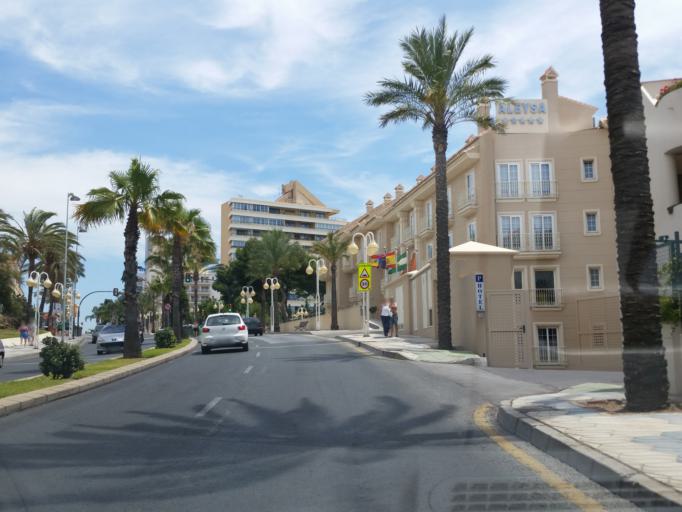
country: ES
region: Andalusia
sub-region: Provincia de Malaga
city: Torremolinos
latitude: 36.5927
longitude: -4.5233
